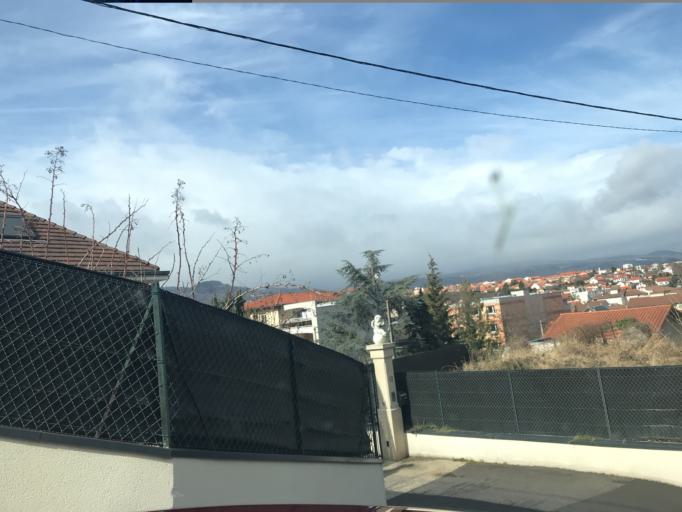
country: FR
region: Auvergne
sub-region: Departement du Puy-de-Dome
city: Aubiere
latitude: 45.7474
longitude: 3.1124
